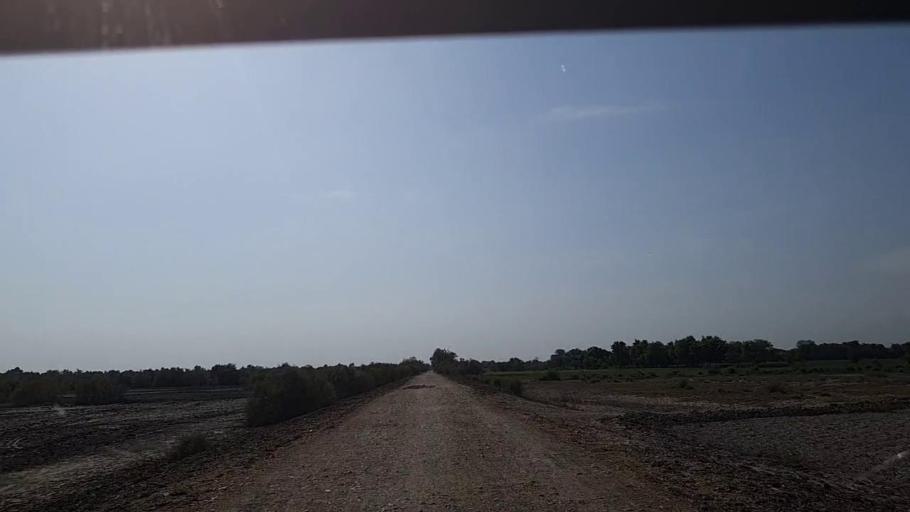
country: PK
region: Sindh
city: Khanpur
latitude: 27.8380
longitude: 69.3198
